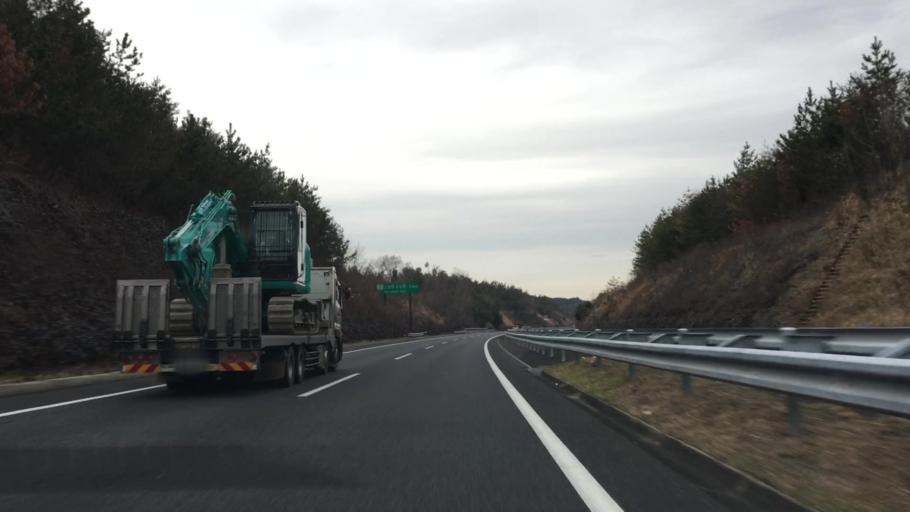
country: JP
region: Gifu
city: Toki
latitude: 35.3124
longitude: 137.1775
